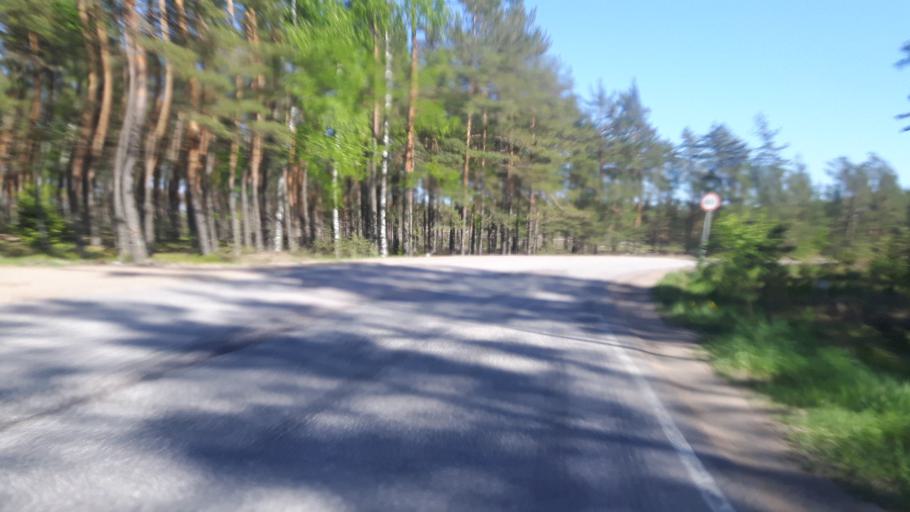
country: RU
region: Leningrad
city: Glebychevo
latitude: 60.2775
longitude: 28.9213
